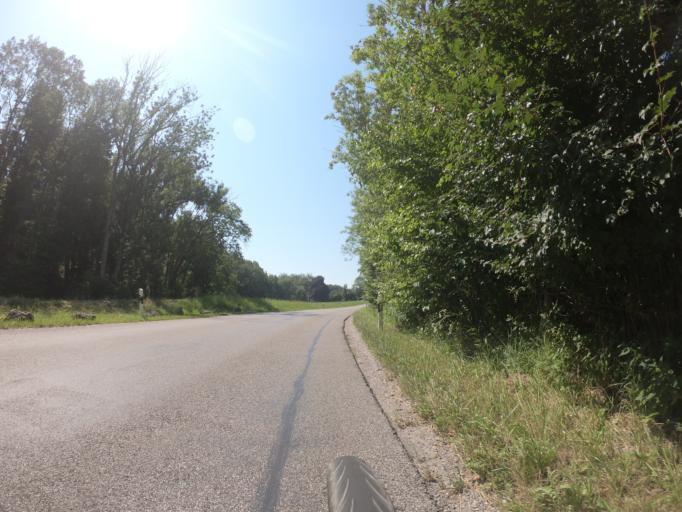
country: DE
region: Bavaria
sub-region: Upper Bavaria
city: Fuerstenfeldbruck
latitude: 48.1630
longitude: 11.2563
